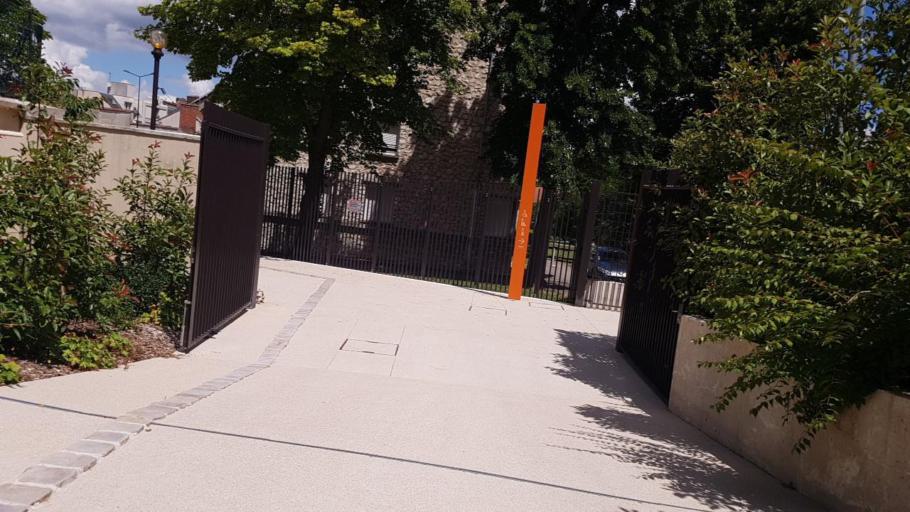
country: FR
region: Champagne-Ardenne
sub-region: Departement de la Marne
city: Magenta
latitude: 49.0440
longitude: 3.9617
